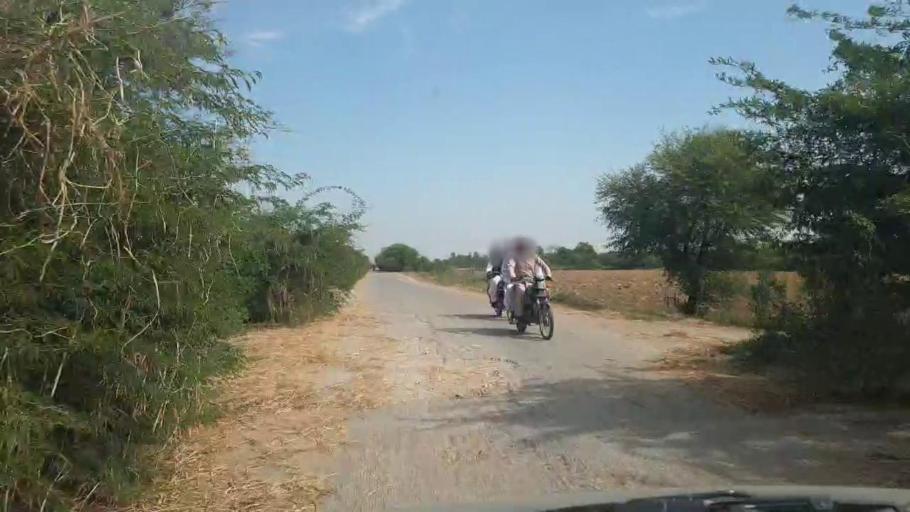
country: PK
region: Sindh
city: Tando Bago
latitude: 24.9013
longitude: 69.0168
